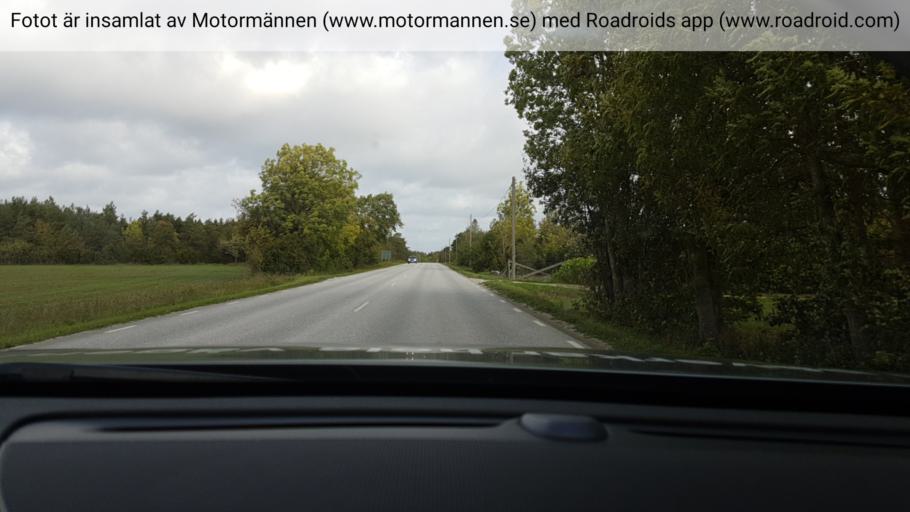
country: SE
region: Gotland
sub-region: Gotland
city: Slite
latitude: 57.7764
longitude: 18.7808
